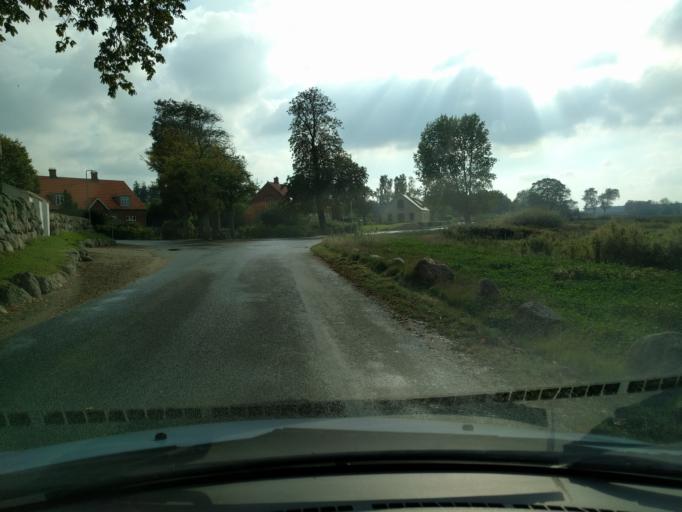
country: DK
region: South Denmark
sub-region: Kerteminde Kommune
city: Munkebo
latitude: 55.4254
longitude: 10.5825
